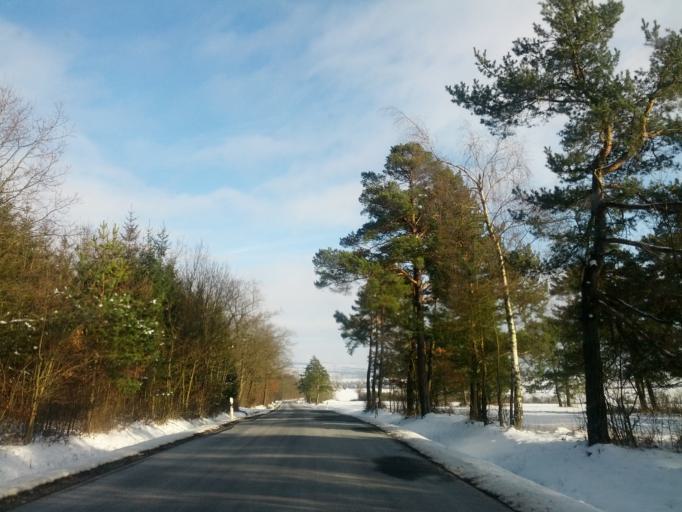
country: DE
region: Thuringia
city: Weberstedt
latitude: 51.0504
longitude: 10.5039
